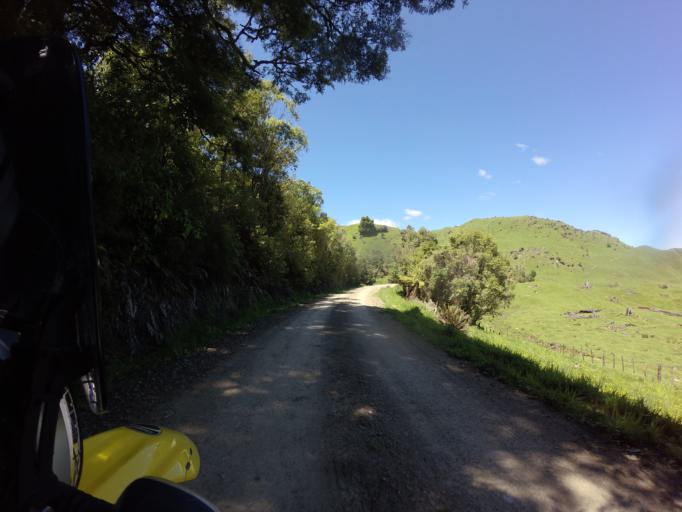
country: NZ
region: Bay of Plenty
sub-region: Opotiki District
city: Opotiki
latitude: -38.4072
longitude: 177.4391
